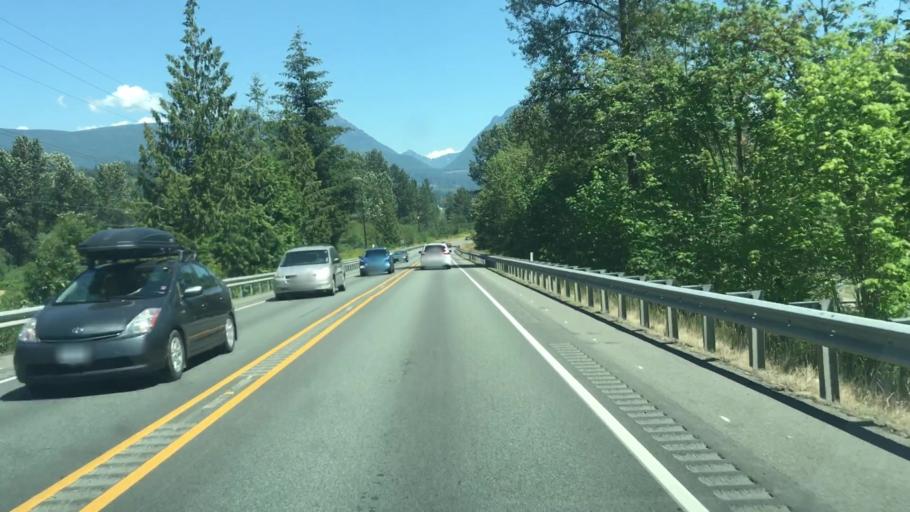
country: US
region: Washington
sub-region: Snohomish County
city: Sultan
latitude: 47.8692
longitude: -121.7679
